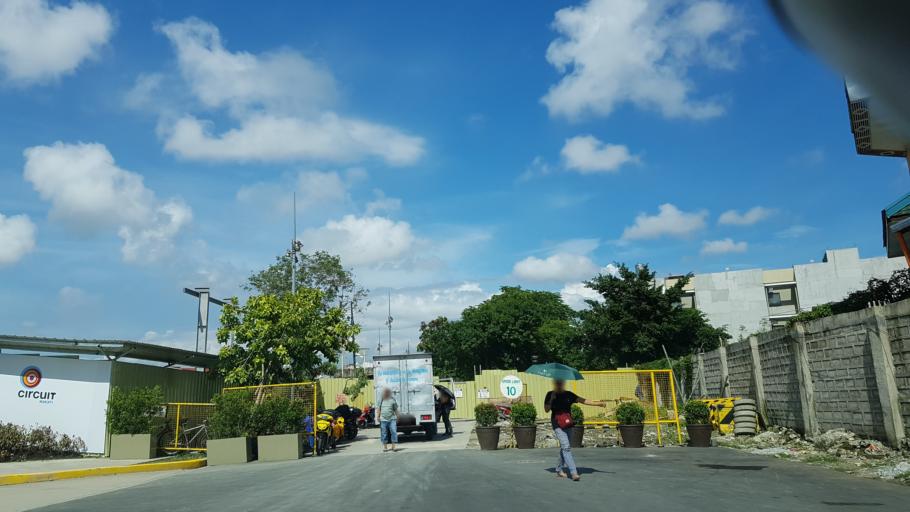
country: PH
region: Metro Manila
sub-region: Mandaluyong
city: Mandaluyong City
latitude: 14.5720
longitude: 121.0196
